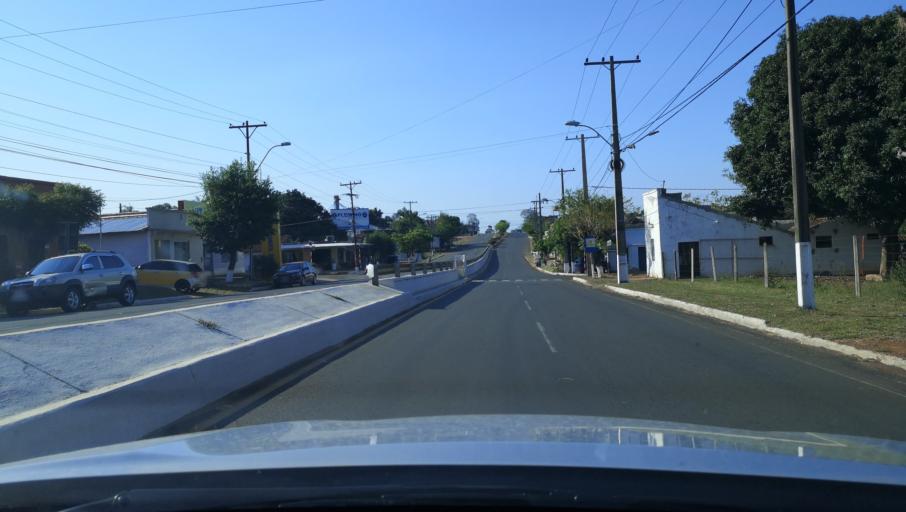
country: PY
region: Misiones
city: Santa Maria
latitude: -26.8838
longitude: -57.0318
